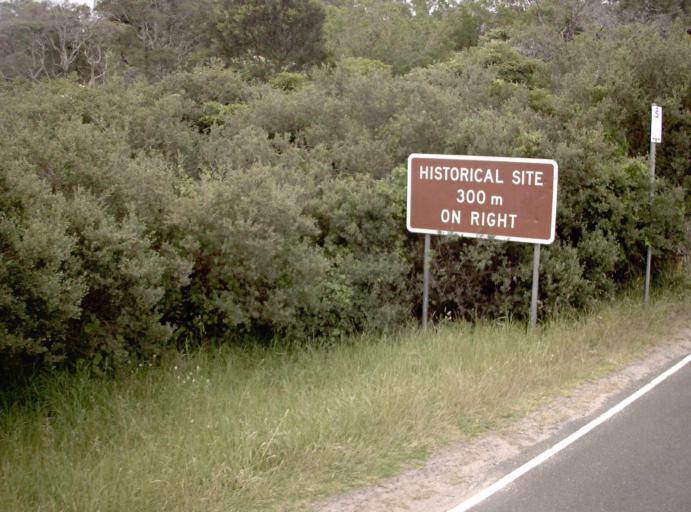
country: AU
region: Victoria
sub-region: Mornington Peninsula
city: Blairgowrie
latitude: -38.3524
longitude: 144.7621
